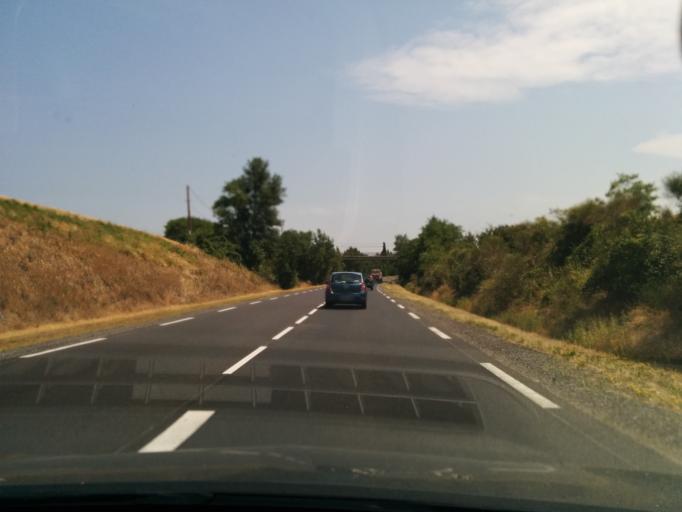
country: FR
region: Midi-Pyrenees
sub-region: Departement de la Haute-Garonne
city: Avignonet-Lauragais
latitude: 43.3489
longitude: 1.8534
